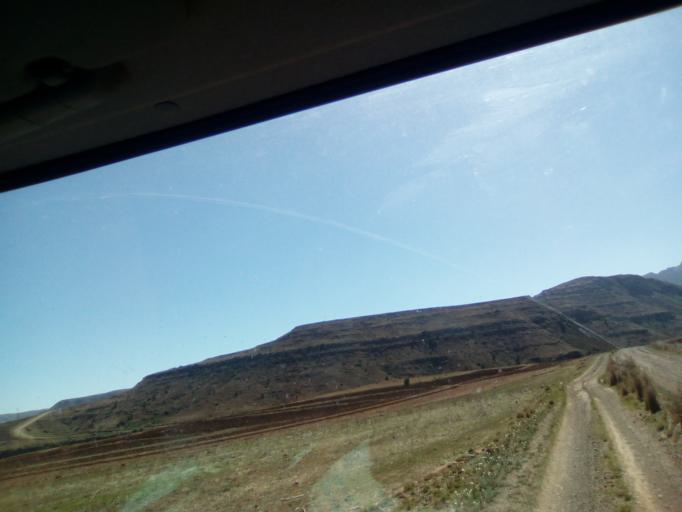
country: LS
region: Qacha's Nek
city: Qacha's Nek
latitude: -30.0593
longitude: 28.6275
